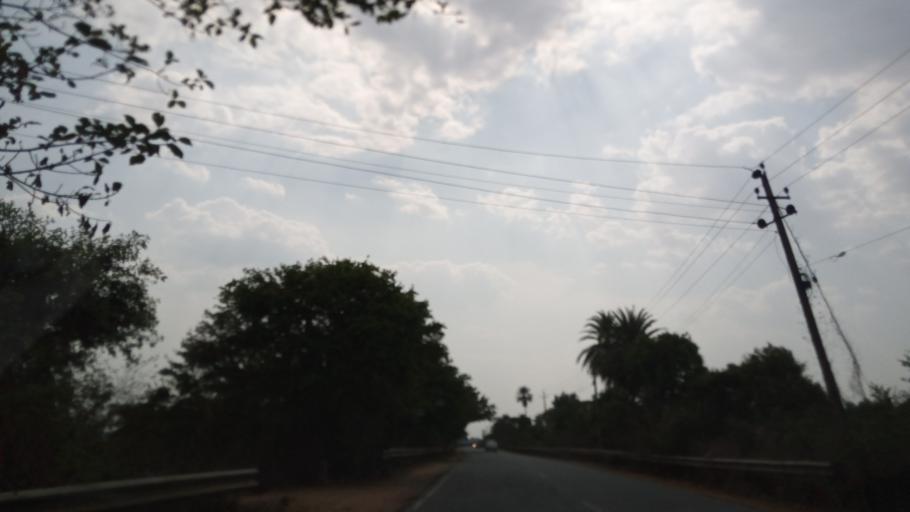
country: IN
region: Karnataka
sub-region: Hassan
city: Belur
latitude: 13.1634
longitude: 75.8883
